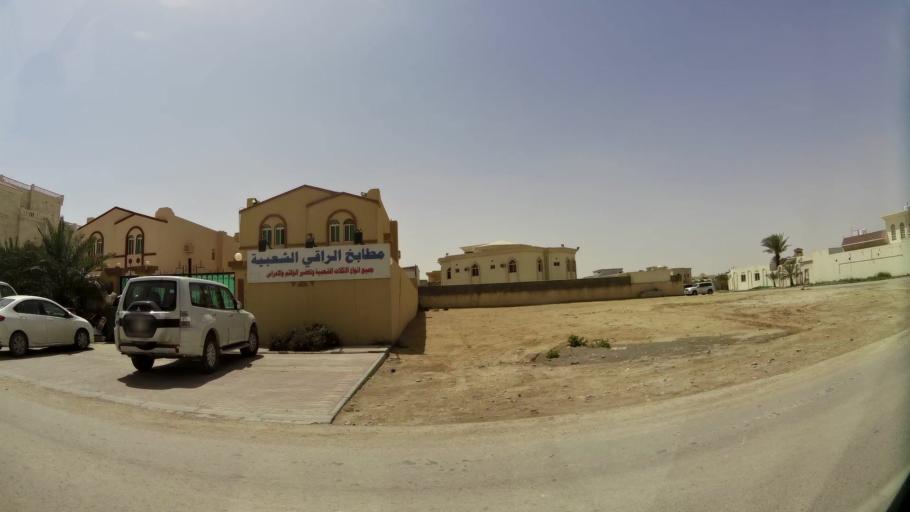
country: QA
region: Baladiyat Umm Salal
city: Umm Salal Muhammad
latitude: 25.3724
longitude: 51.4544
